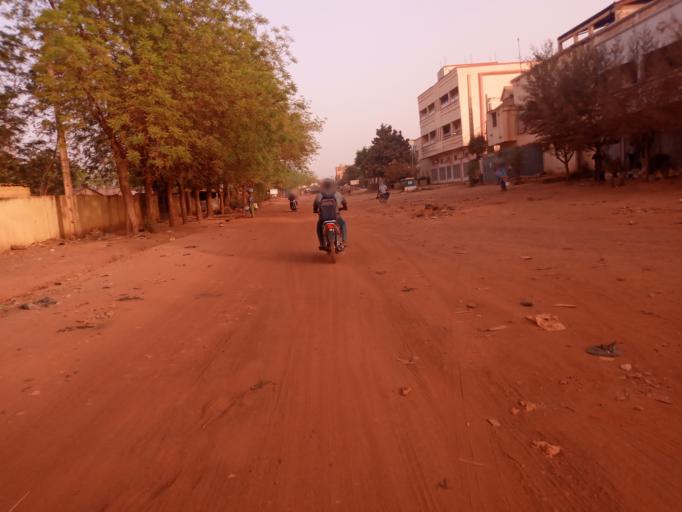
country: ML
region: Bamako
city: Bamako
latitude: 12.5946
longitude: -7.9610
